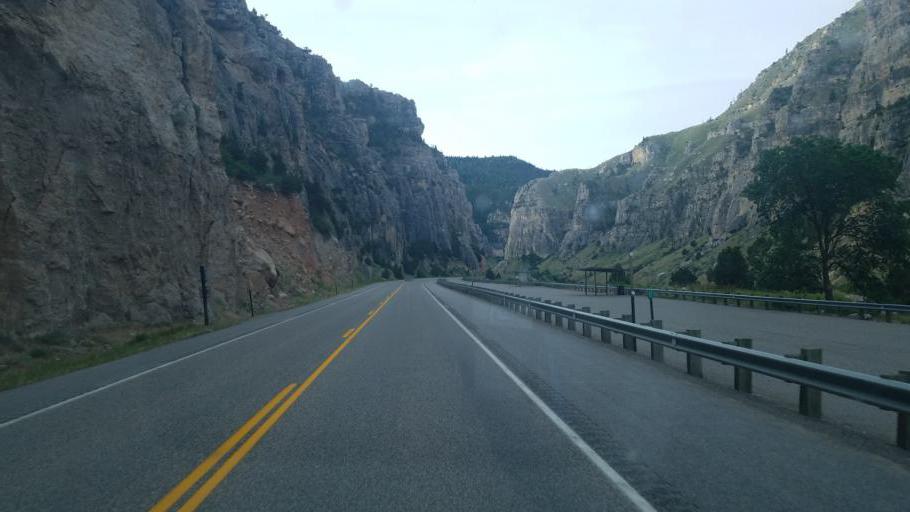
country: US
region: Wyoming
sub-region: Hot Springs County
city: Thermopolis
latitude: 43.5378
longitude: -108.1800
